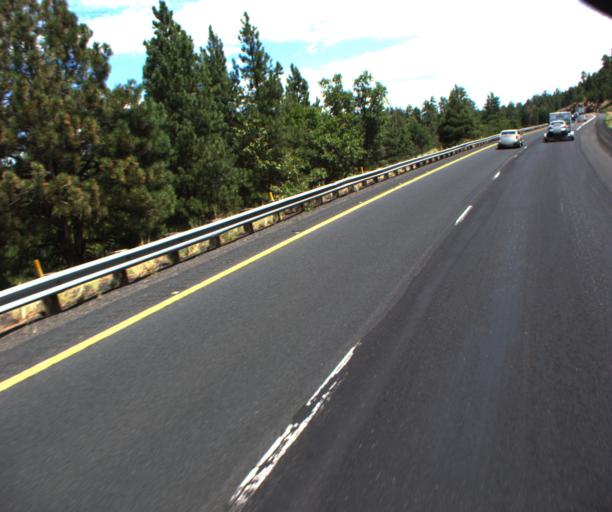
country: US
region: Arizona
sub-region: Yavapai County
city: Village of Oak Creek (Big Park)
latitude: 34.8227
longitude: -111.6113
